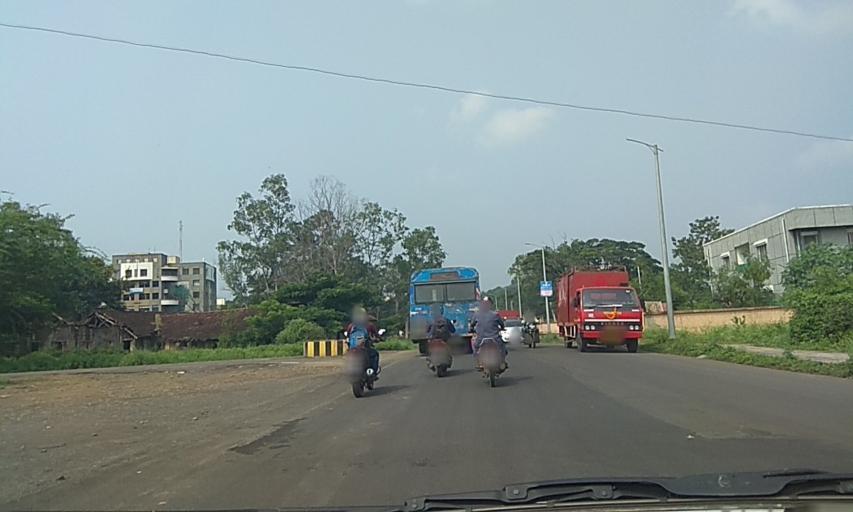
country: IN
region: Maharashtra
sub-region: Pune Division
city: Shivaji Nagar
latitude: 18.5449
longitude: 73.8403
